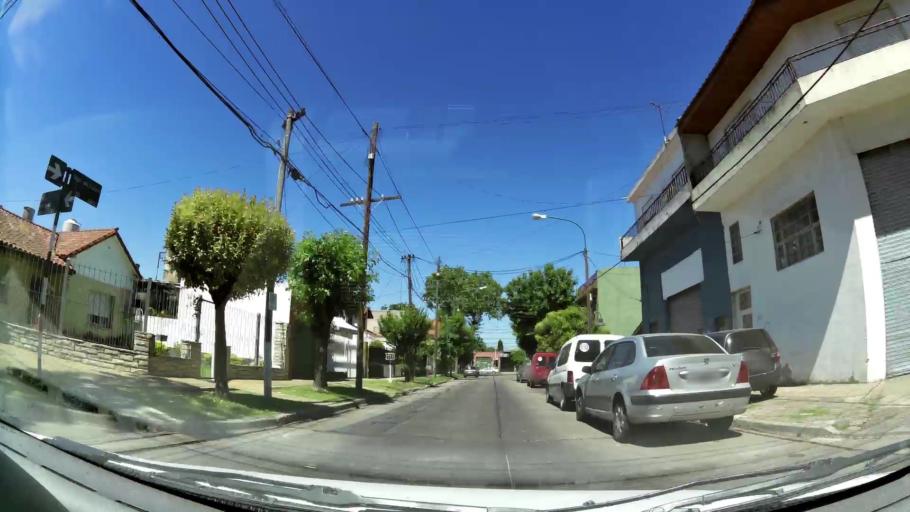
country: AR
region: Buenos Aires
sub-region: Partido de General San Martin
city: General San Martin
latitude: -34.5314
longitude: -58.5512
